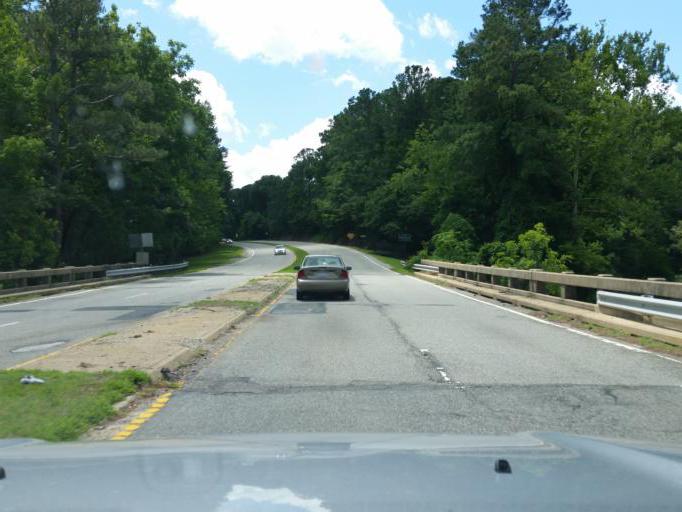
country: US
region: Virginia
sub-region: City of Williamsburg
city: Williamsburg
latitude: 37.2931
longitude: -76.6869
